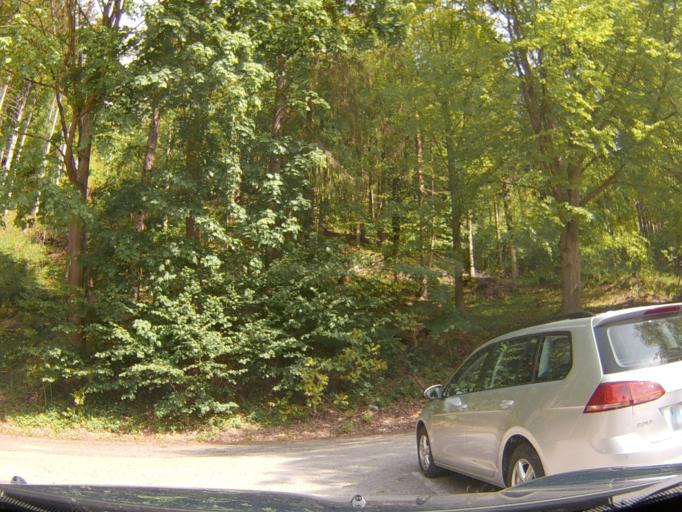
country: AT
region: Tyrol
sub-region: Politischer Bezirk Schwaz
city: Buch bei Jenbach
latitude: 47.3822
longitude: 11.7394
